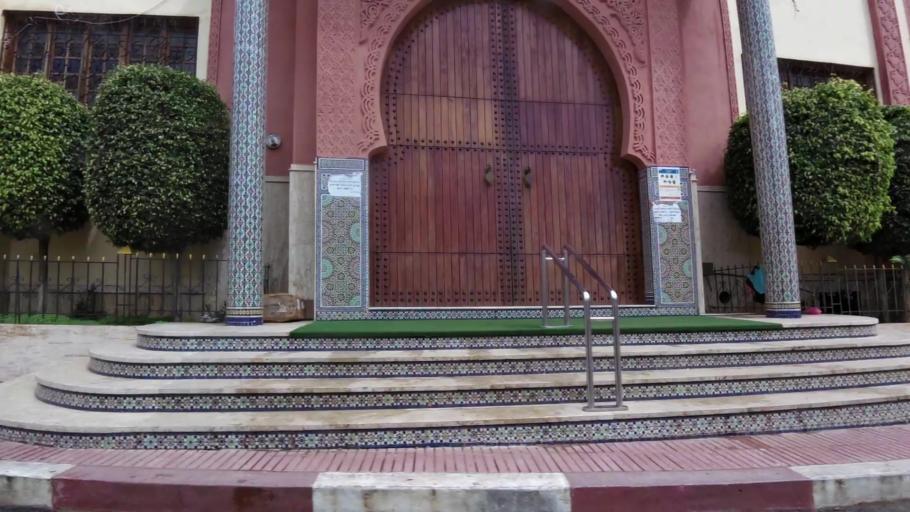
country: MA
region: Grand Casablanca
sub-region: Casablanca
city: Casablanca
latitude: 33.5349
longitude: -7.6510
